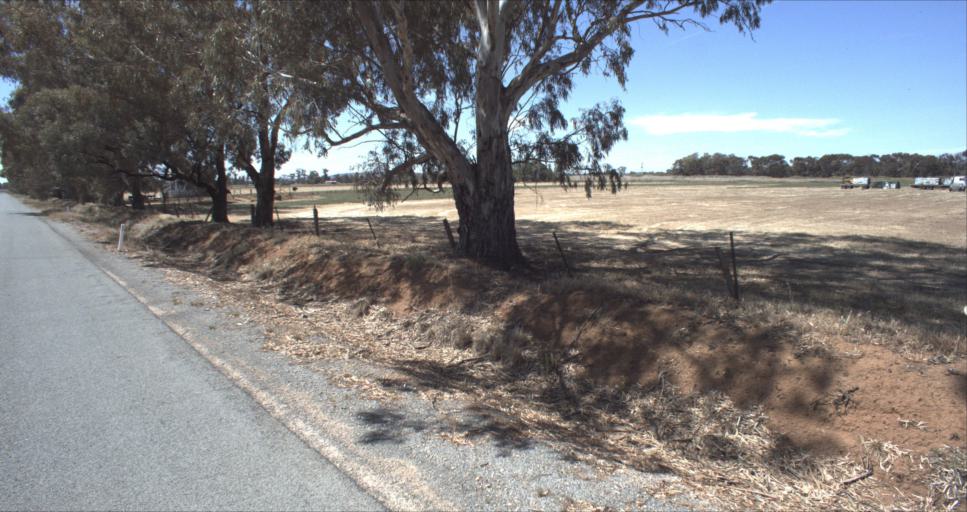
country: AU
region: New South Wales
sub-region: Leeton
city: Leeton
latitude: -34.5798
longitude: 146.4207
